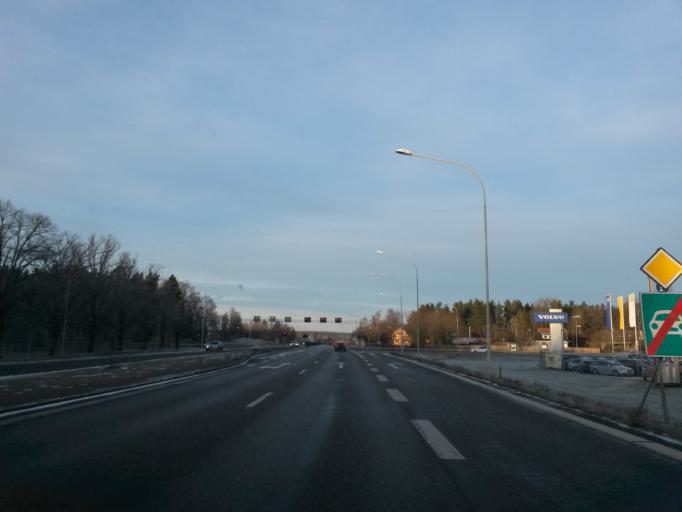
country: SE
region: Vaestra Goetaland
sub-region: Vanersborgs Kommun
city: Vanersborg
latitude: 58.3552
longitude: 12.3143
